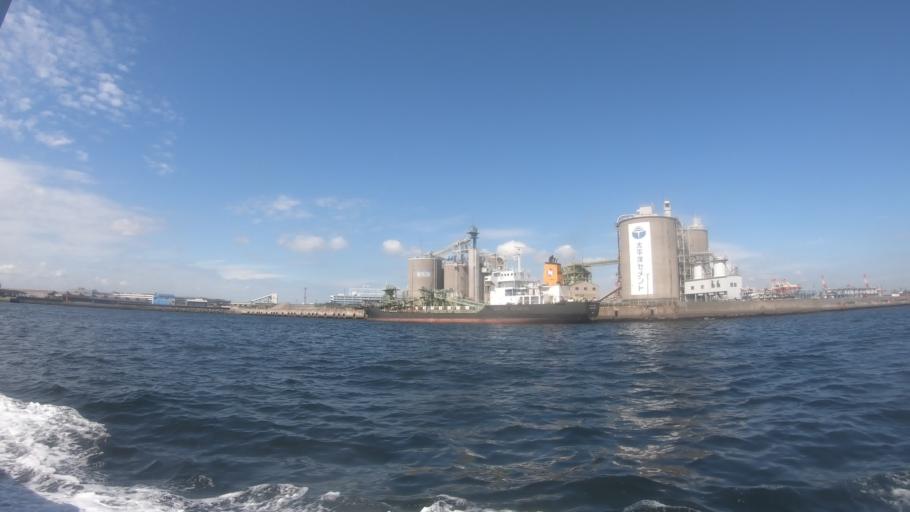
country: JP
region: Kanagawa
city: Yokohama
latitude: 35.4257
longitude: 139.6861
